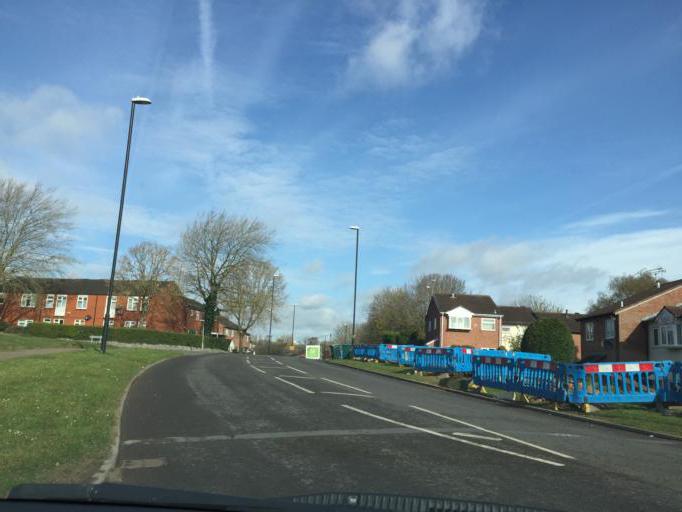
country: GB
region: England
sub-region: Coventry
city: Coventry
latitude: 52.3867
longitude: -1.4963
